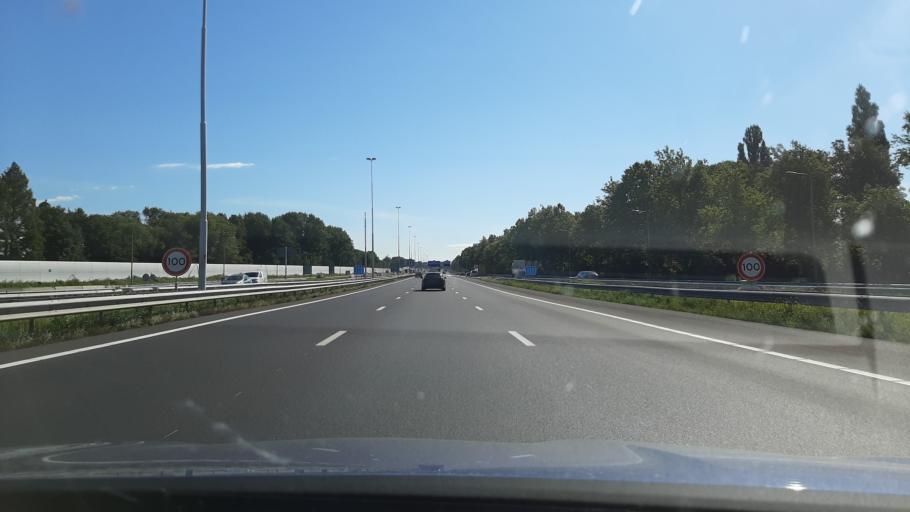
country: NL
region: South Holland
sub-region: Gemeente Rotterdam
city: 's-Gravenland
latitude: 51.9510
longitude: 4.5359
